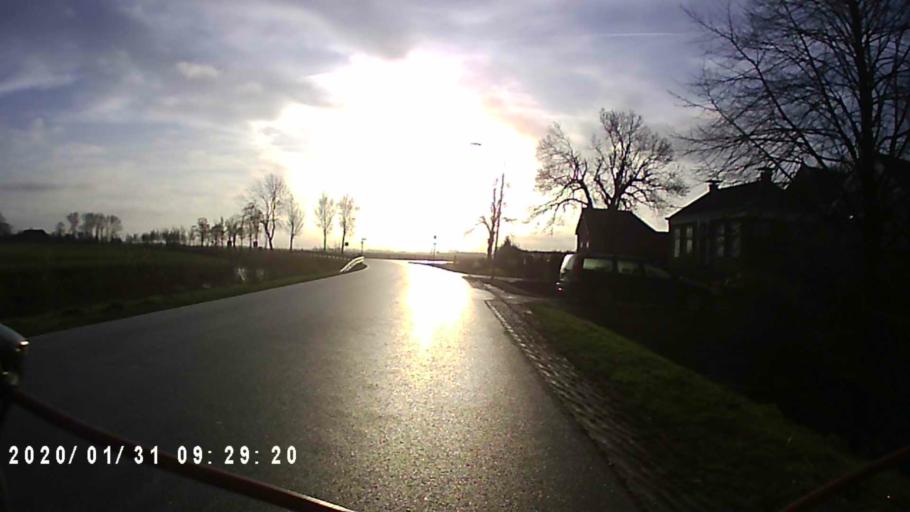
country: NL
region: Groningen
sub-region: Gemeente Zuidhorn
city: Aduard
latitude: 53.3051
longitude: 6.4479
